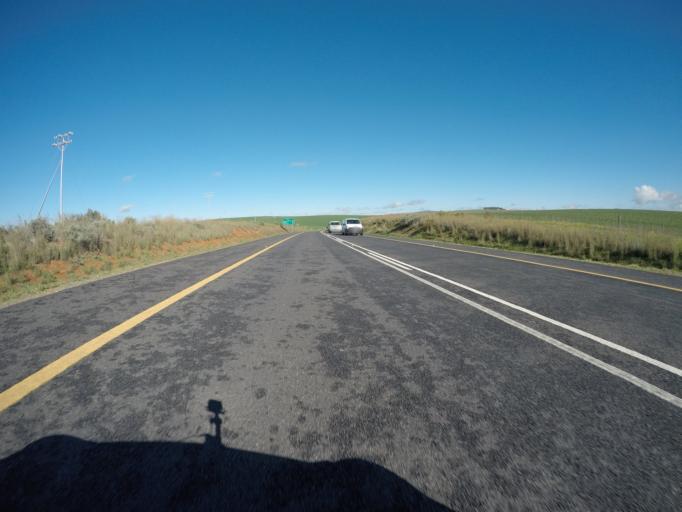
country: ZA
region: Western Cape
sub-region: Overberg District Municipality
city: Swellendam
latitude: -34.0803
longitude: 20.4030
